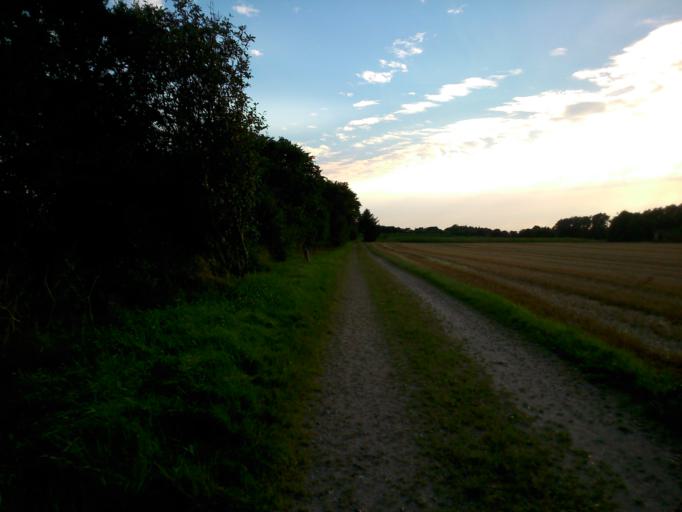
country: DK
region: Central Jutland
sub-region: Ringkobing-Skjern Kommune
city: Tarm
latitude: 55.9471
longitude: 8.6221
